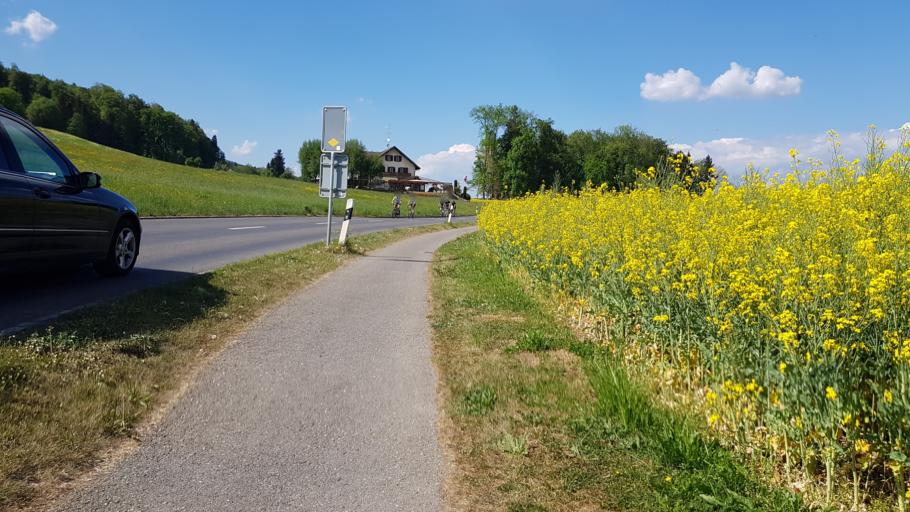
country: CH
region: Lucerne
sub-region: Hochdorf District
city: Roemerswil
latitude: 47.1938
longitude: 8.2528
